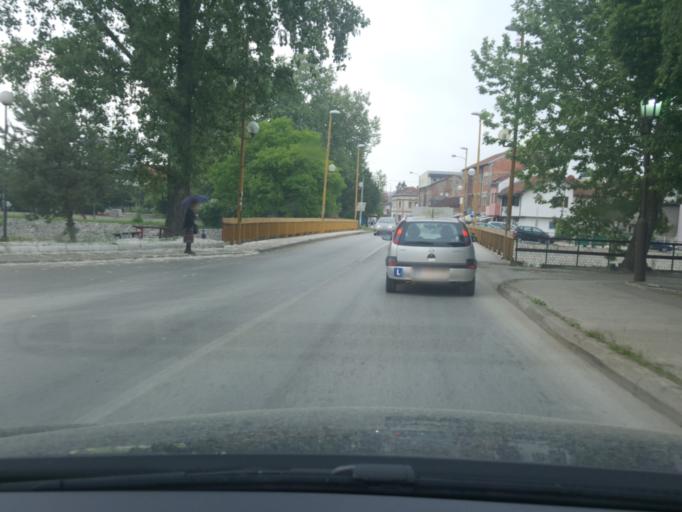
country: RS
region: Central Serbia
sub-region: Kolubarski Okrug
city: Valjevo
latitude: 44.2685
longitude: 19.8801
